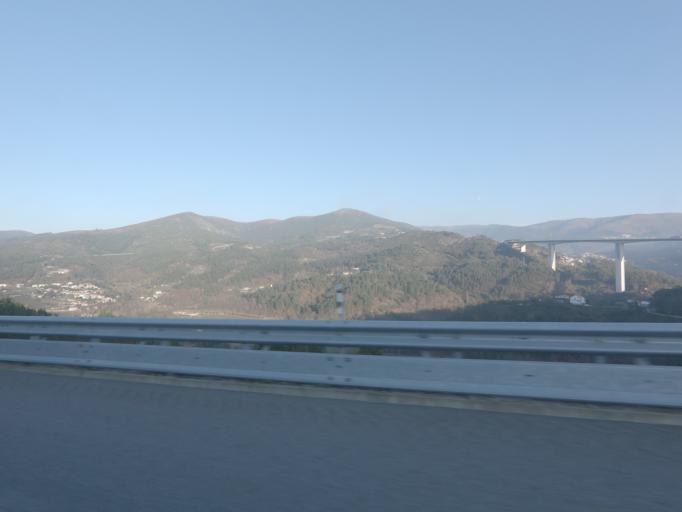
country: PT
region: Porto
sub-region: Amarante
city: Amarante
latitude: 41.2541
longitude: -7.9954
